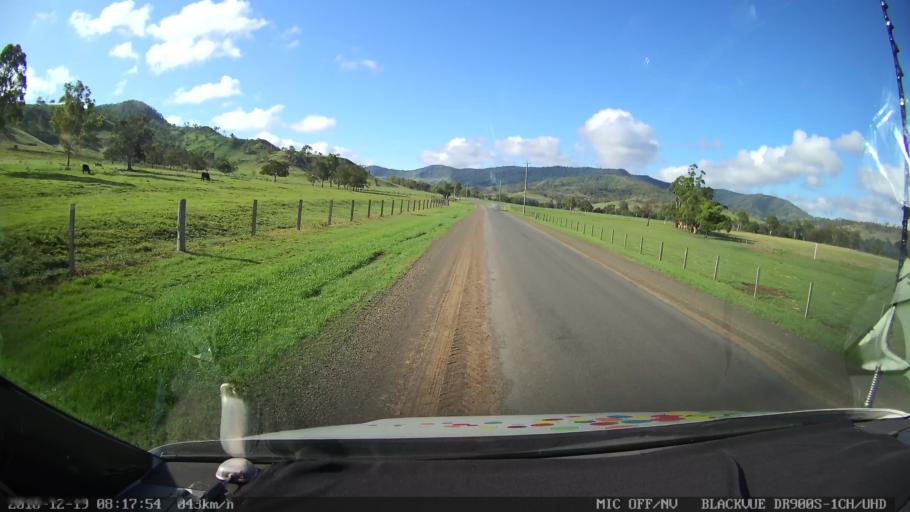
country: AU
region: New South Wales
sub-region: Kyogle
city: Kyogle
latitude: -28.2694
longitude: 152.9099
